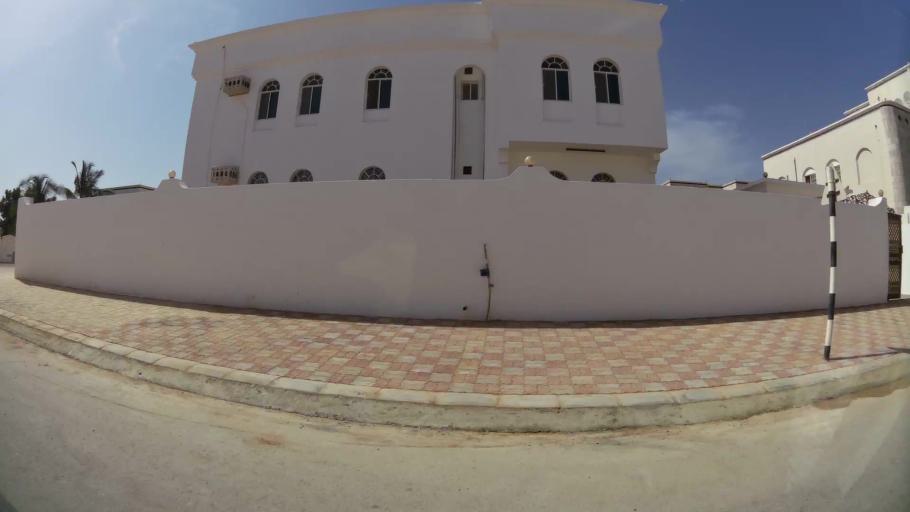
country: OM
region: Zufar
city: Salalah
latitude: 17.0457
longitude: 54.1500
